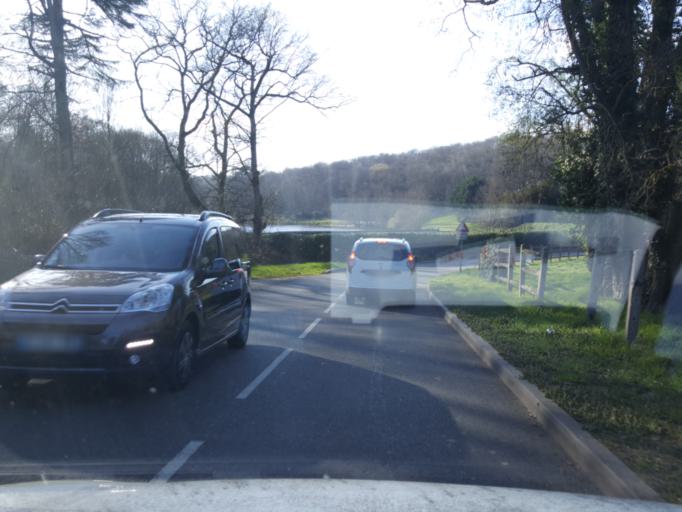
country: FR
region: Ile-de-France
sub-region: Departement des Yvelines
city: Gazeran
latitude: 48.6341
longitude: 1.7668
